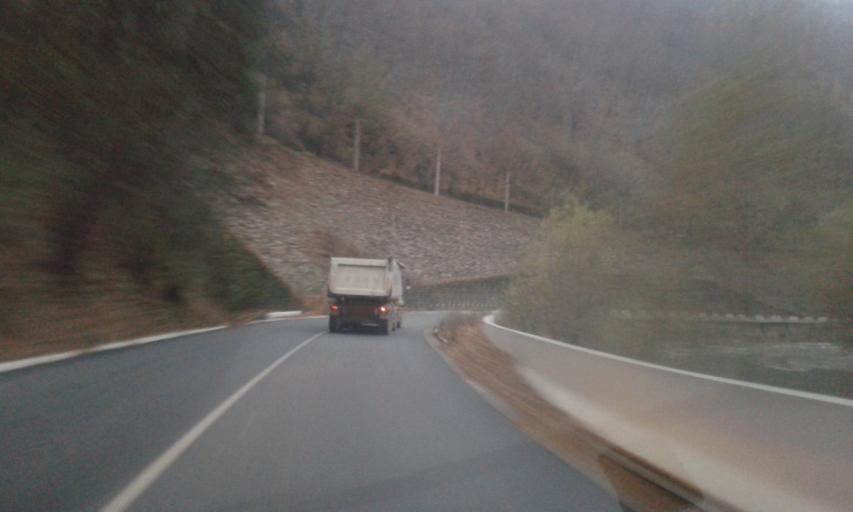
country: RO
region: Gorj
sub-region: Comuna Bumbesti-Jiu
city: Bumbesti-Jiu
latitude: 45.2286
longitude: 23.3890
